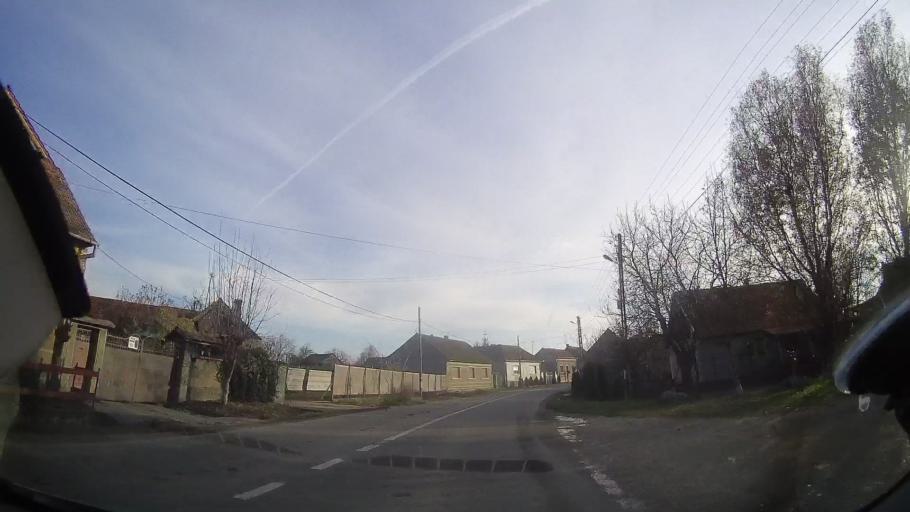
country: RO
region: Bihor
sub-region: Comuna Tileagd
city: Tileagd
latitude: 47.0609
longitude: 22.2444
